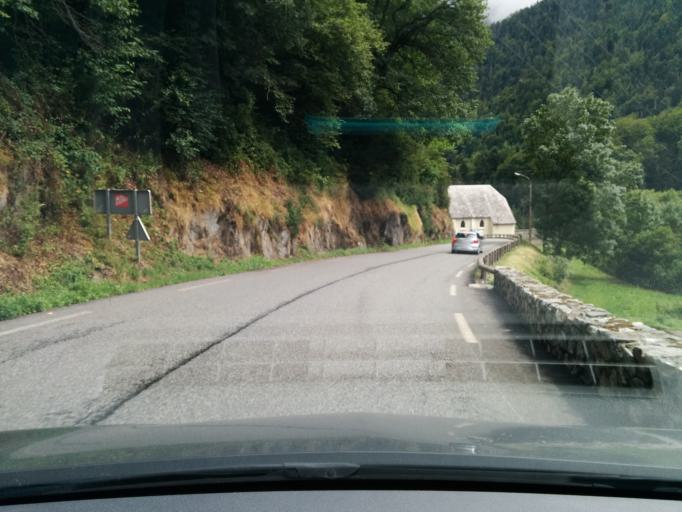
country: FR
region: Midi-Pyrenees
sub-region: Departement des Hautes-Pyrenees
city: Saint-Lary-Soulan
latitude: 42.7898
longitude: 0.2300
